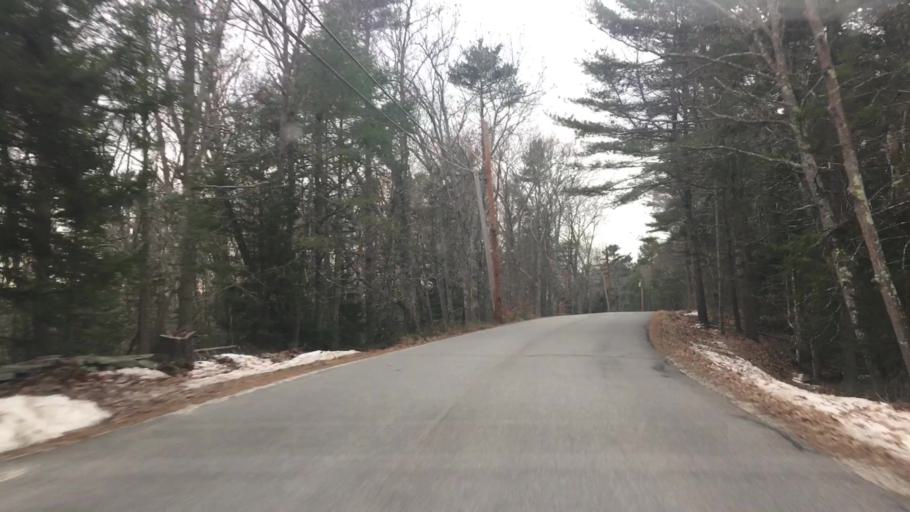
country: US
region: Maine
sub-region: Cumberland County
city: Freeport
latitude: 43.8407
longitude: -70.0726
